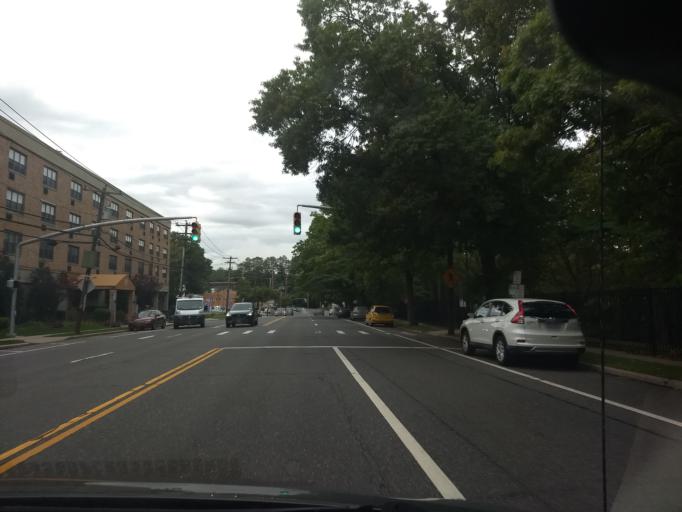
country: US
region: New York
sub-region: Nassau County
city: Thomaston
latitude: 40.7895
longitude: -73.7077
